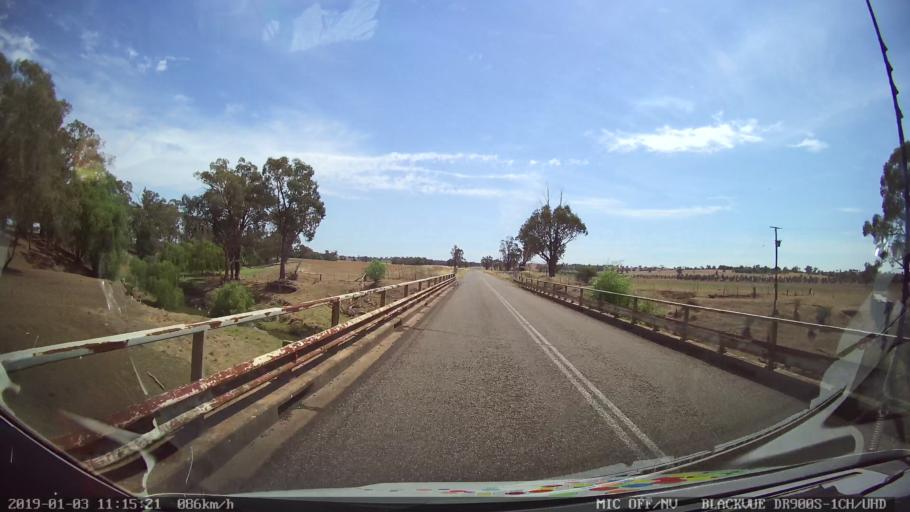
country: AU
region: New South Wales
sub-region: Young
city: Young
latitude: -34.1649
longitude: 148.2639
